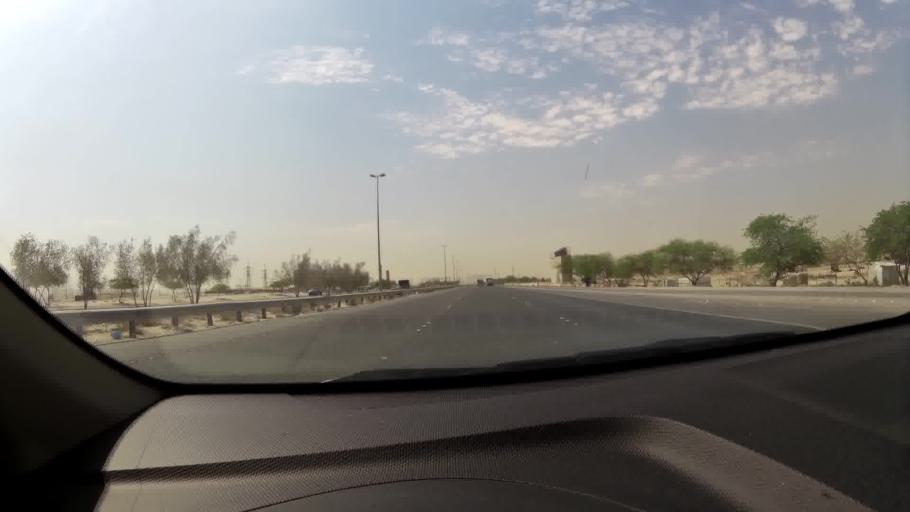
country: KW
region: Al Ahmadi
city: Al Fahahil
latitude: 28.7475
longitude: 48.2824
